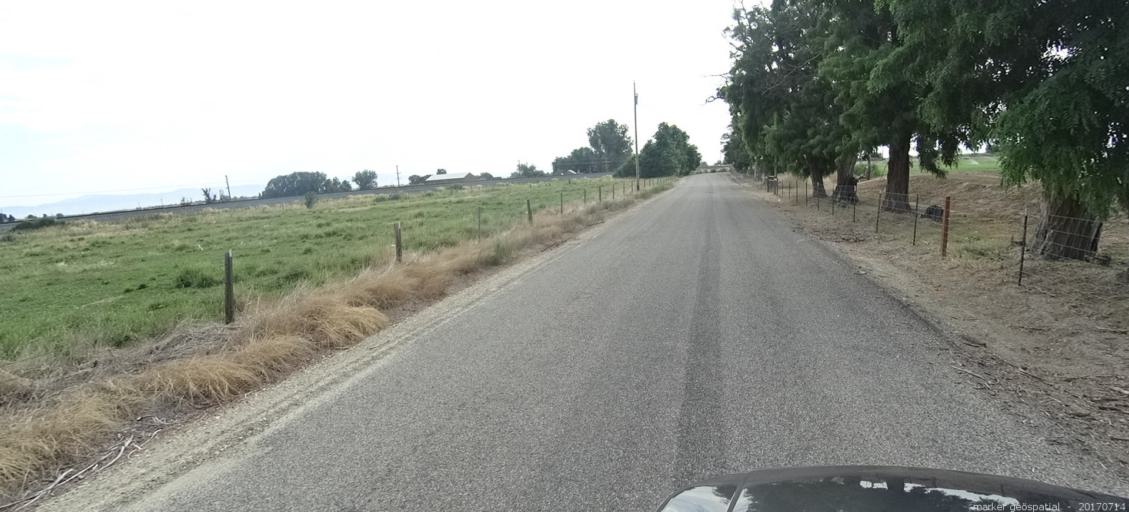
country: US
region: Idaho
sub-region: Ada County
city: Kuna
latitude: 43.4593
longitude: -116.3583
